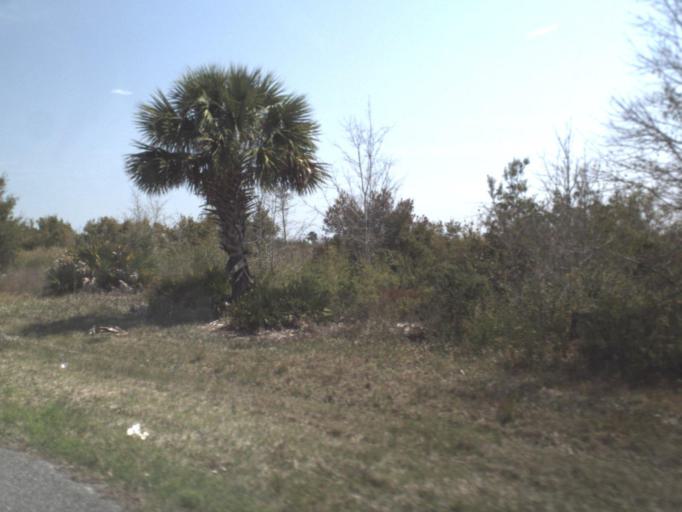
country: US
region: Florida
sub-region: Franklin County
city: Apalachicola
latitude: 29.7207
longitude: -85.0685
